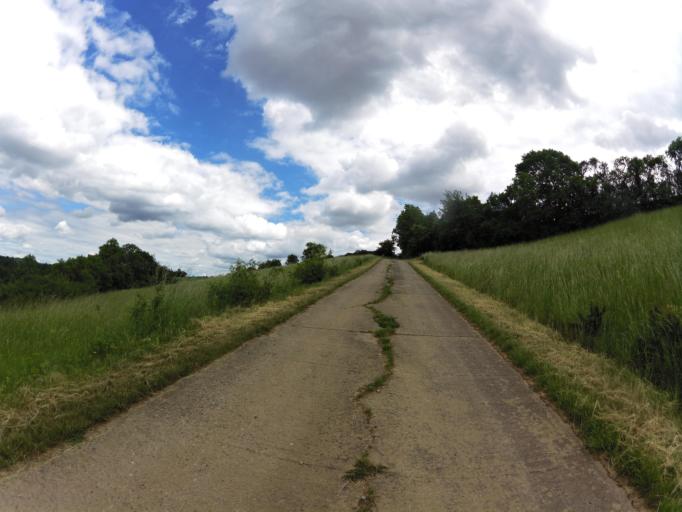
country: DE
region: Bavaria
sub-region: Regierungsbezirk Unterfranken
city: Winterhausen
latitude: 49.6728
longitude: 10.0049
